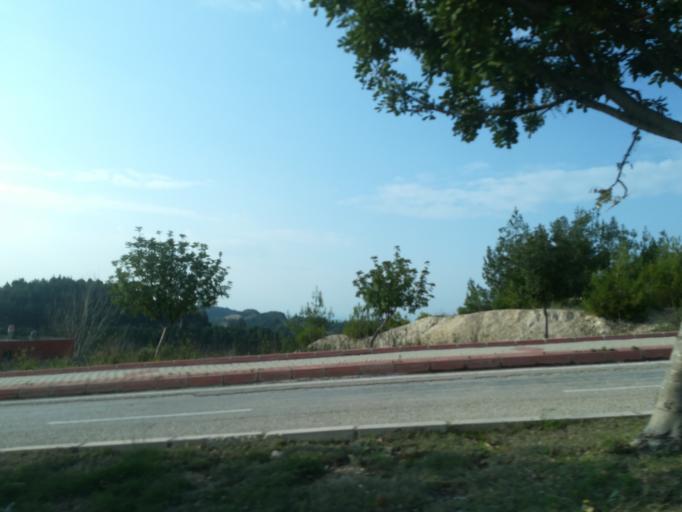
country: TR
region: Adana
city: Adana
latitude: 37.0683
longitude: 35.3769
